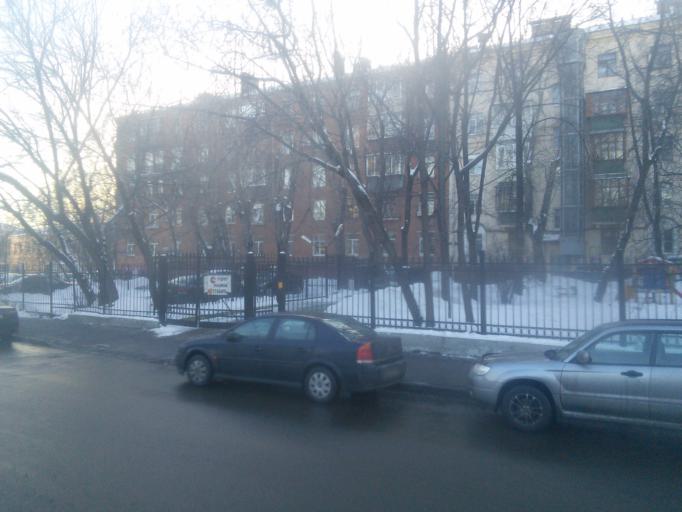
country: RU
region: Moscow
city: Lefortovo
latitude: 55.7644
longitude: 37.6709
